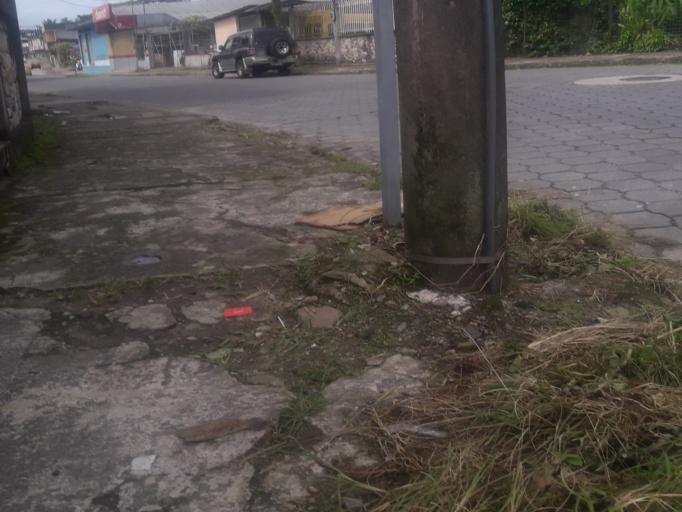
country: EC
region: Napo
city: Tena
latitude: -0.9962
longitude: -77.8115
